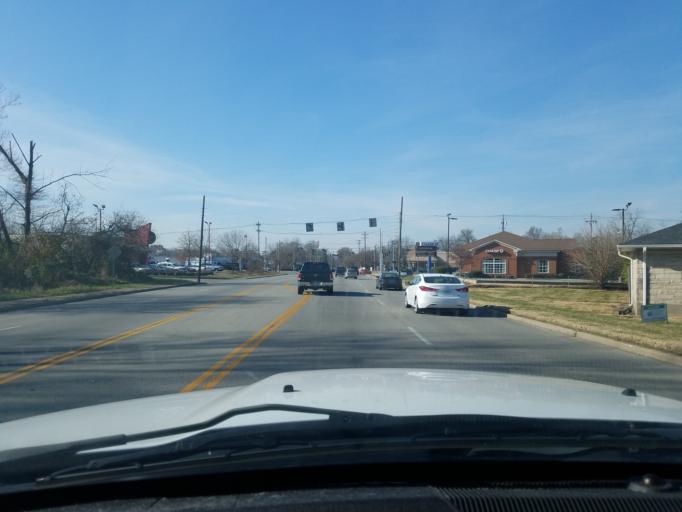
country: US
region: Kentucky
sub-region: Jefferson County
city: Pleasure Ridge Park
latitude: 38.1434
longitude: -85.8378
